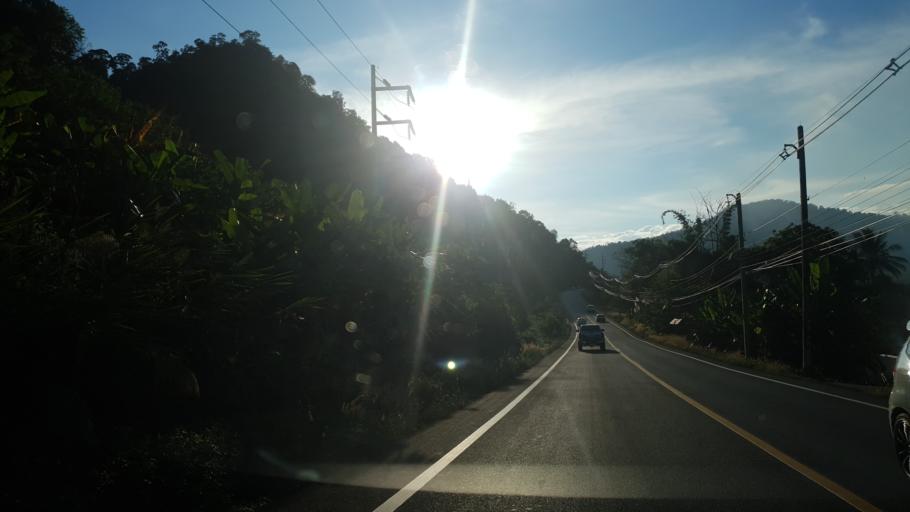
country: TH
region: Loei
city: Dan Sai
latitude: 17.2288
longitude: 101.0440
